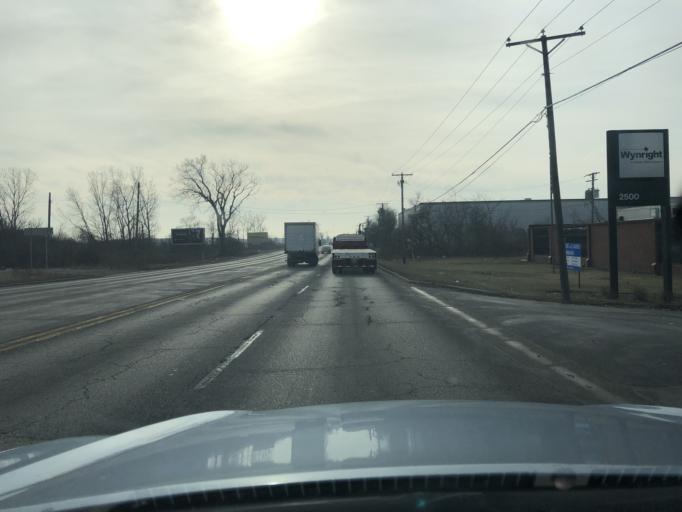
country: US
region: Illinois
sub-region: Cook County
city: Elk Grove Village
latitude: 41.9912
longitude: -87.9400
